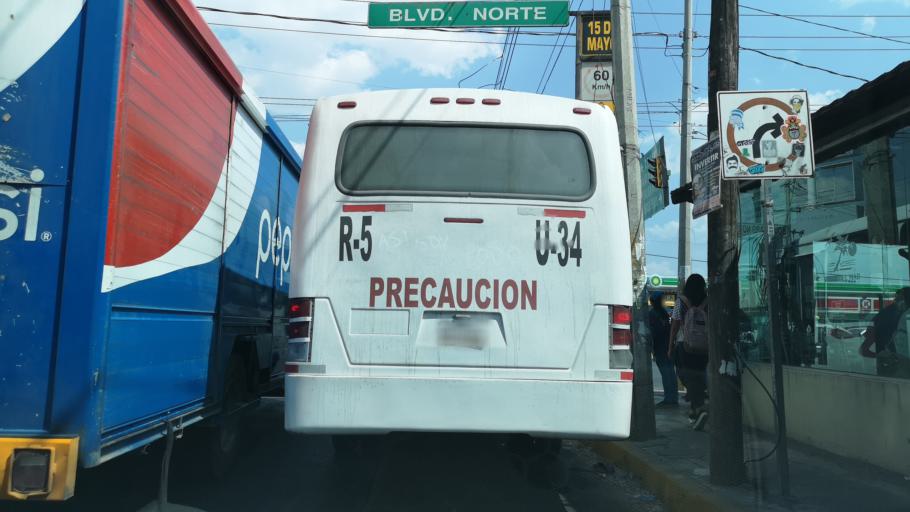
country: MX
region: Puebla
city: Puebla
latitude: 19.0651
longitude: -98.2147
